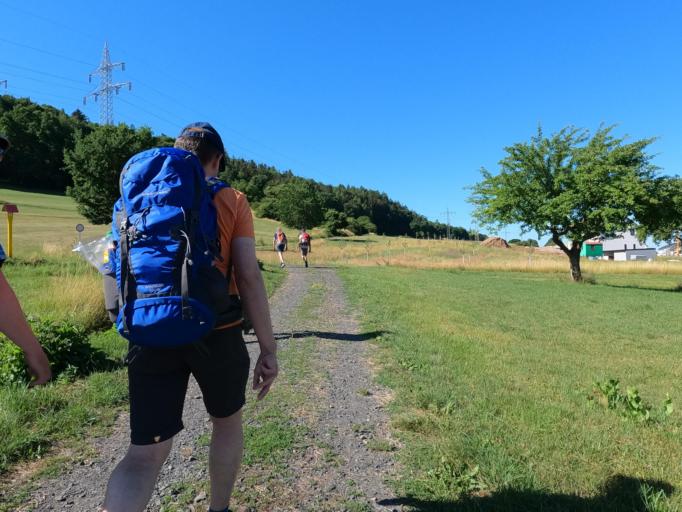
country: DE
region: Hesse
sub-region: Regierungsbezirk Darmstadt
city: Schluchtern
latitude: 50.3424
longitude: 9.5324
